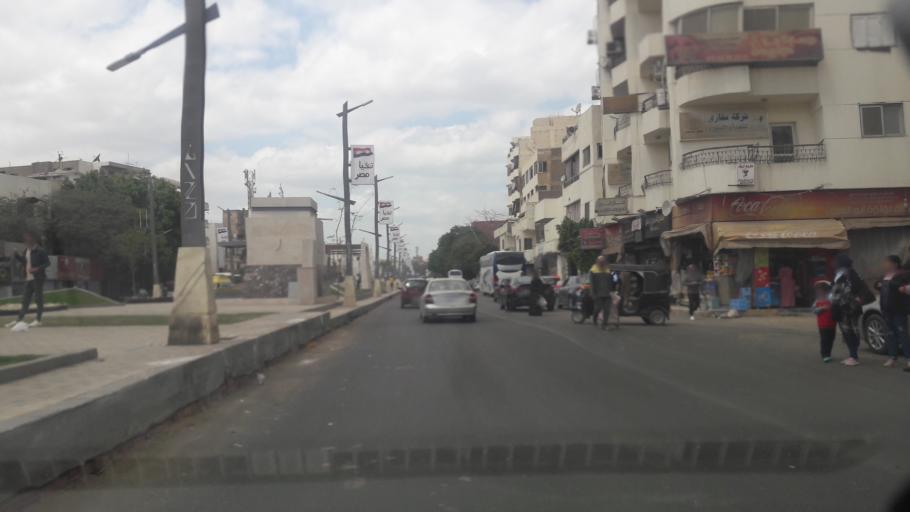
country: EG
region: Al Jizah
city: Al Jizah
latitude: 29.9791
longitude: 31.1440
